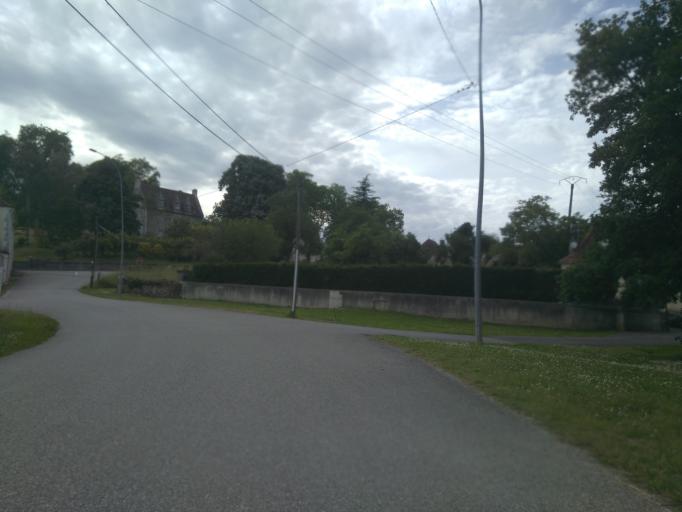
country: FR
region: Aquitaine
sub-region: Departement des Pyrenees-Atlantiques
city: Orthez
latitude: 43.4520
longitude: -0.7725
